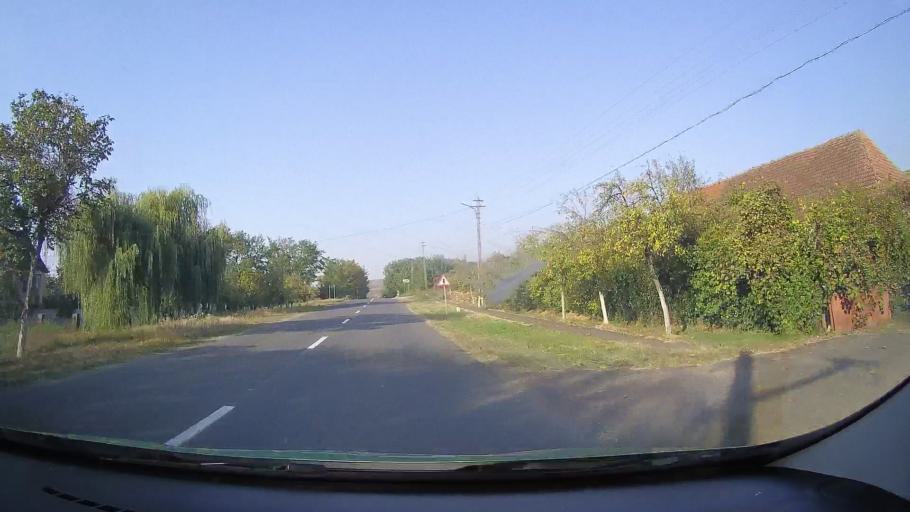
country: RO
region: Arad
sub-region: Comuna Paulis
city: Paulis
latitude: 46.1260
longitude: 21.5993
